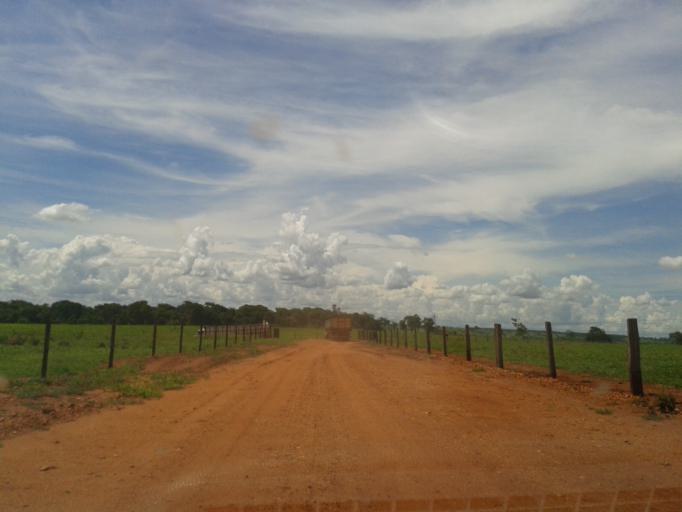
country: BR
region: Minas Gerais
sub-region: Santa Vitoria
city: Santa Vitoria
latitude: -19.1479
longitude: -50.5640
